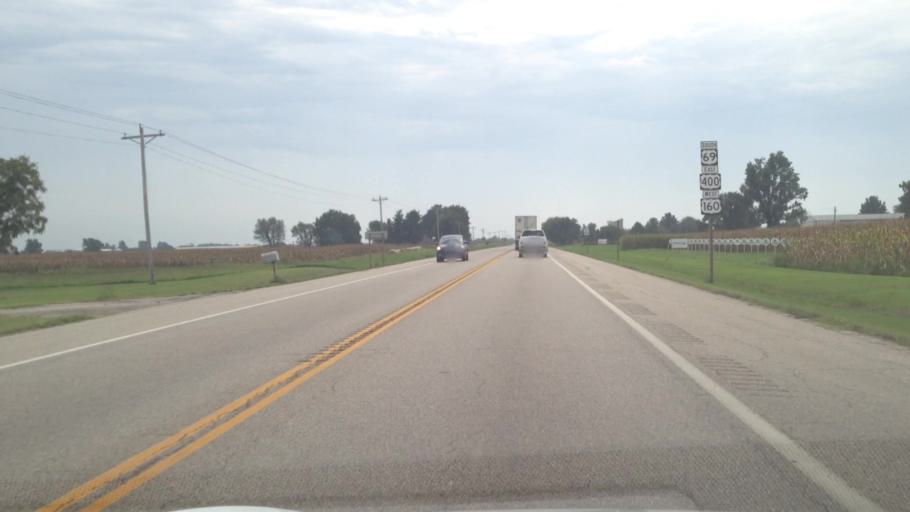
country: US
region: Kansas
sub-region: Crawford County
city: Pittsburg
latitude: 37.2805
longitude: -94.7054
